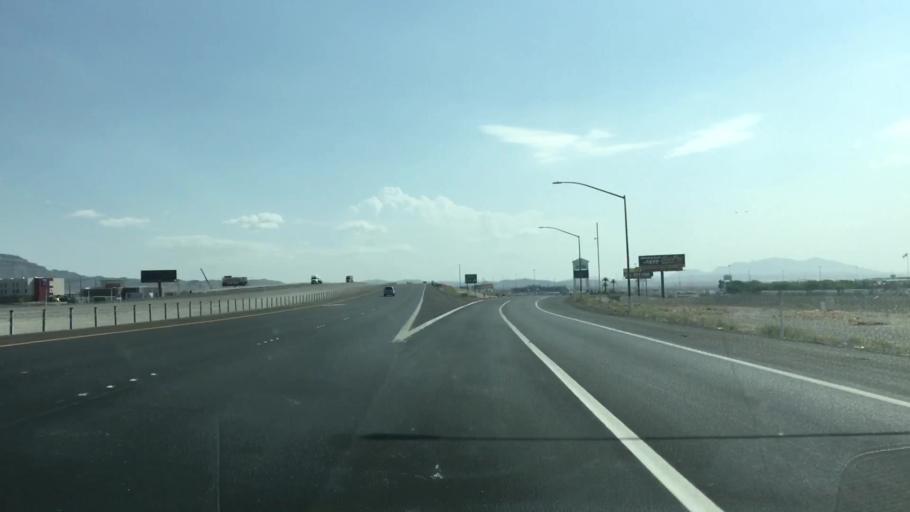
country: US
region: Nevada
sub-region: Clark County
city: Nellis Air Force Base
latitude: 36.2796
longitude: -115.0324
